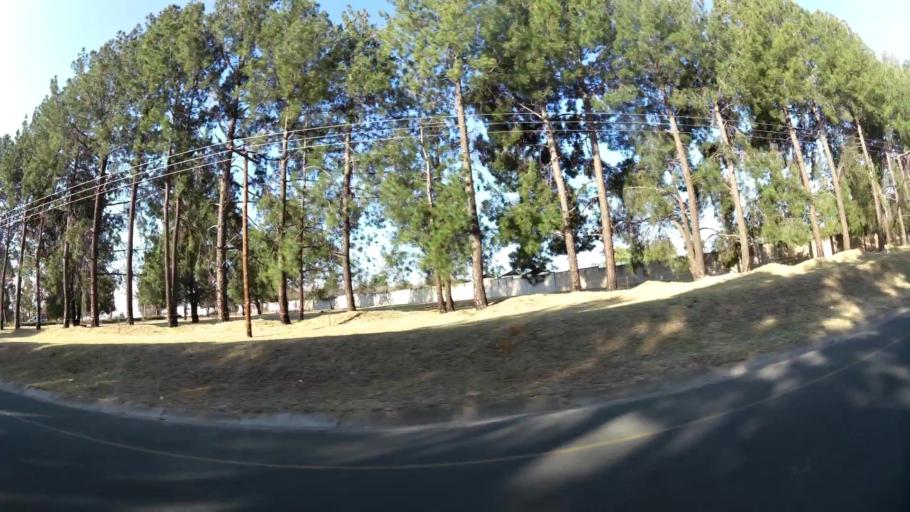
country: ZA
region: Gauteng
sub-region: West Rand District Municipality
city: Muldersdriseloop
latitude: -26.0280
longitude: 27.9085
